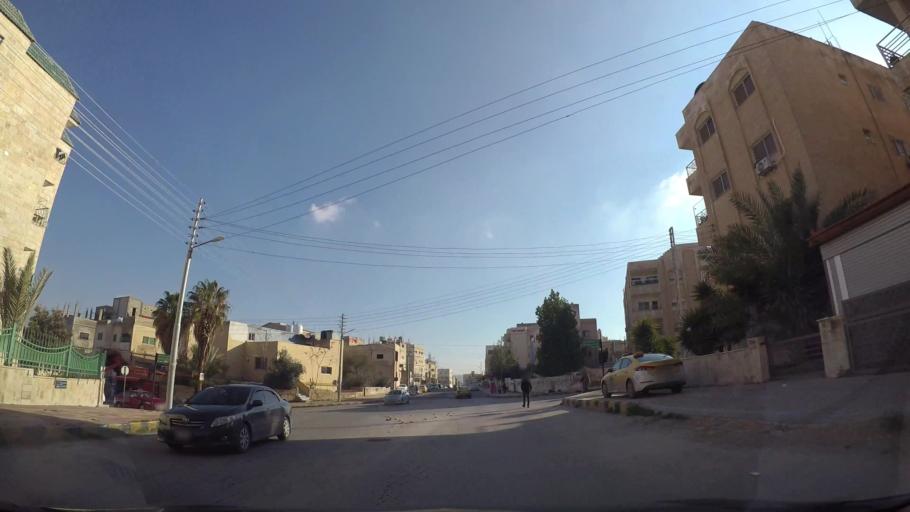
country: JO
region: Amman
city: Amman
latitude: 31.9778
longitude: 35.9600
